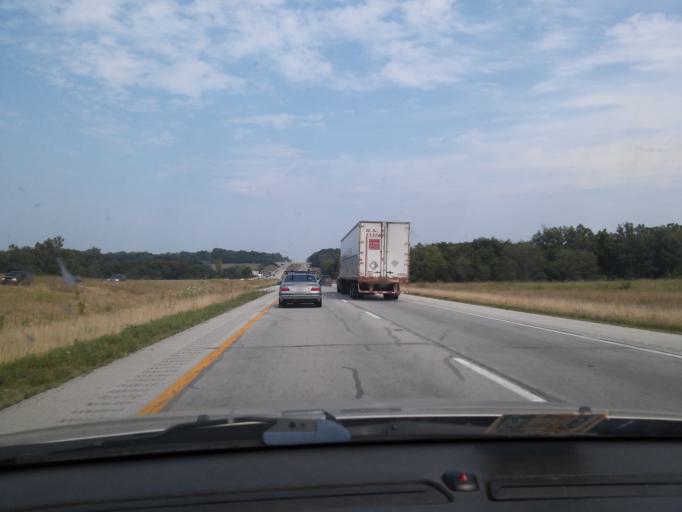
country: US
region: Ohio
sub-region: Preble County
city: Lewisburg
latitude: 39.8372
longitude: -84.5392
